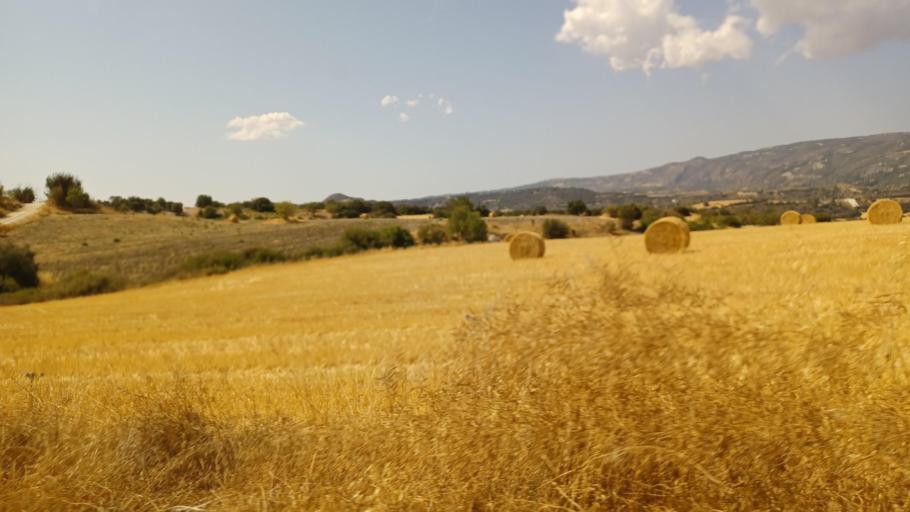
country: CY
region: Pafos
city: Polis
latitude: 34.9712
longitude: 32.4906
